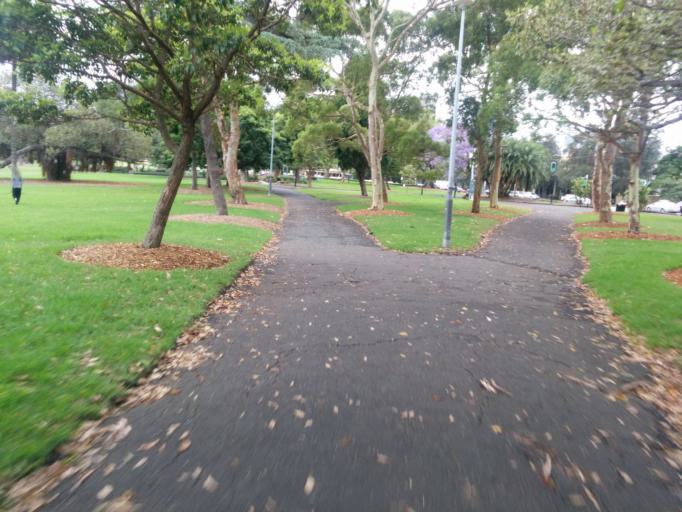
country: AU
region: New South Wales
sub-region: City of Sydney
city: Darlington
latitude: -33.8880
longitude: 151.1920
